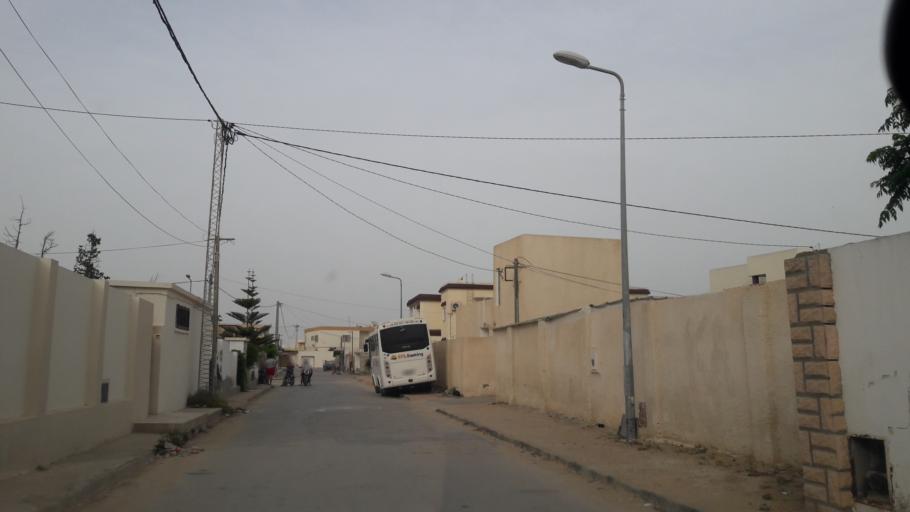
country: TN
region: Safaqis
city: Al Qarmadah
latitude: 34.7771
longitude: 10.7649
